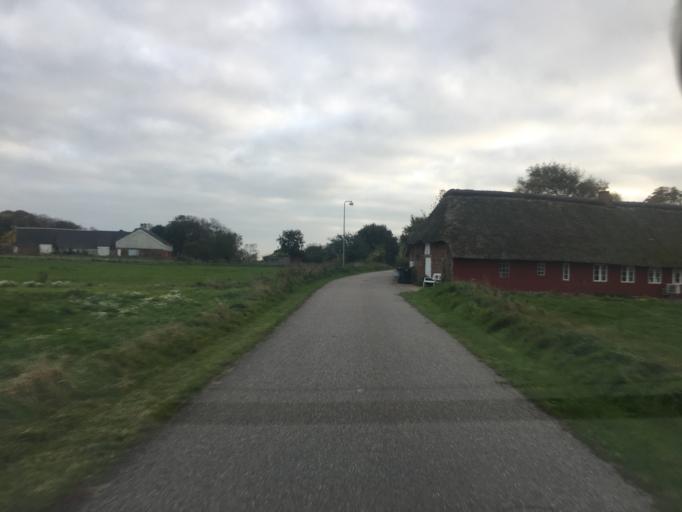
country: DE
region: Schleswig-Holstein
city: Rodenas
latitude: 54.9683
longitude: 8.7382
